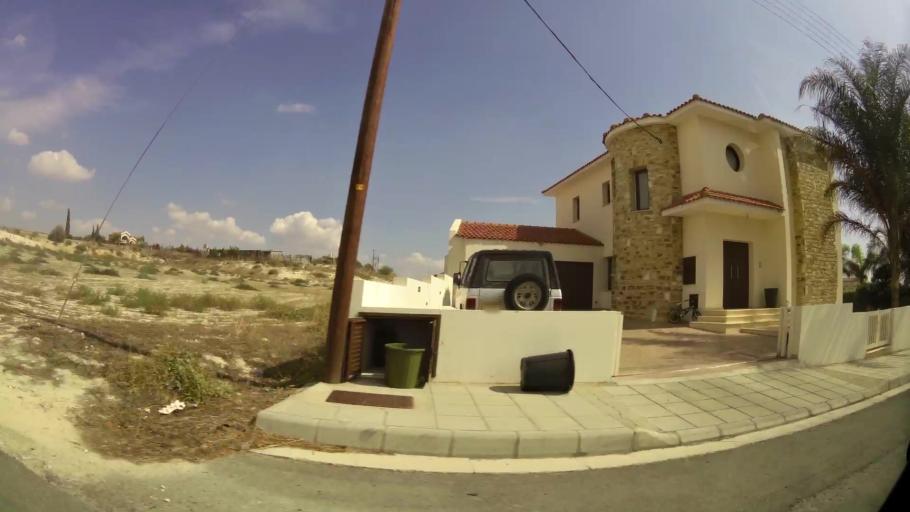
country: CY
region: Larnaka
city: Aradippou
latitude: 34.9600
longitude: 33.5722
